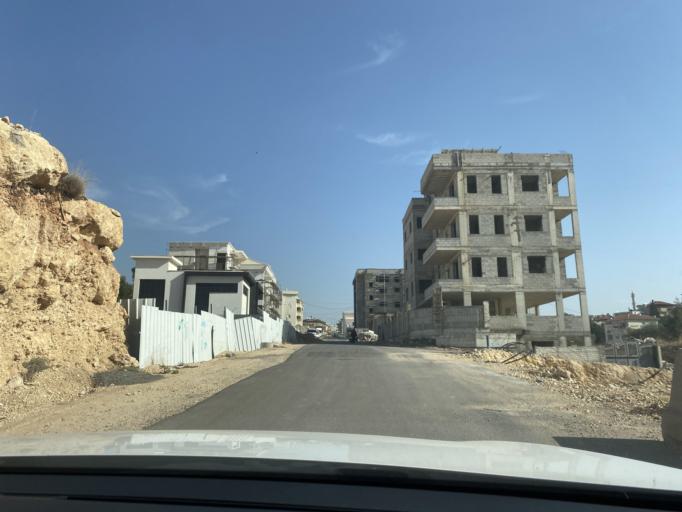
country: IL
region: Central District
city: Kafr Qasim
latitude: 32.1336
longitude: 34.9690
